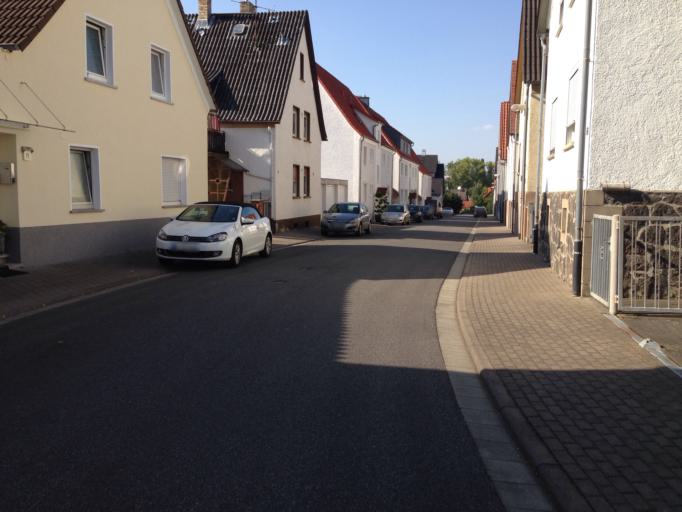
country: DE
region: Hesse
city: Staufenberg
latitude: 50.6472
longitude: 8.7387
